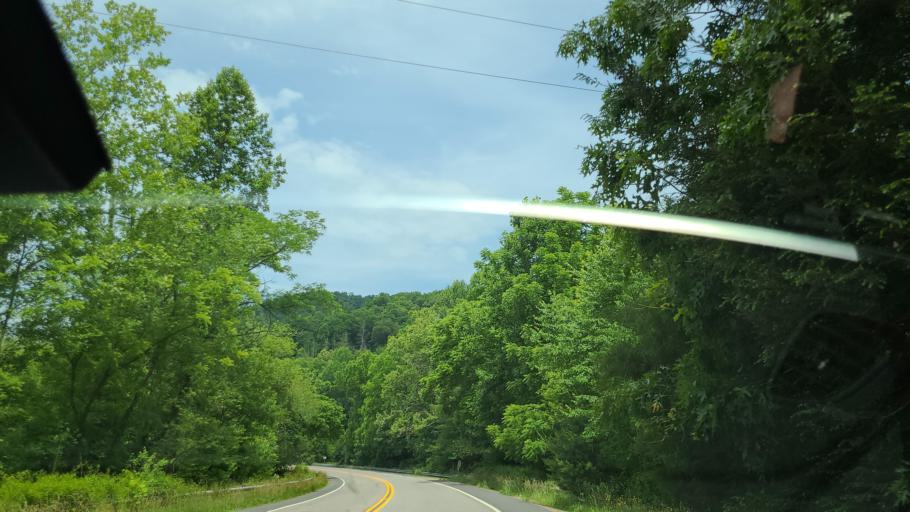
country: US
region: North Carolina
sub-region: Macon County
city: Franklin
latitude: 35.1415
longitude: -83.2872
